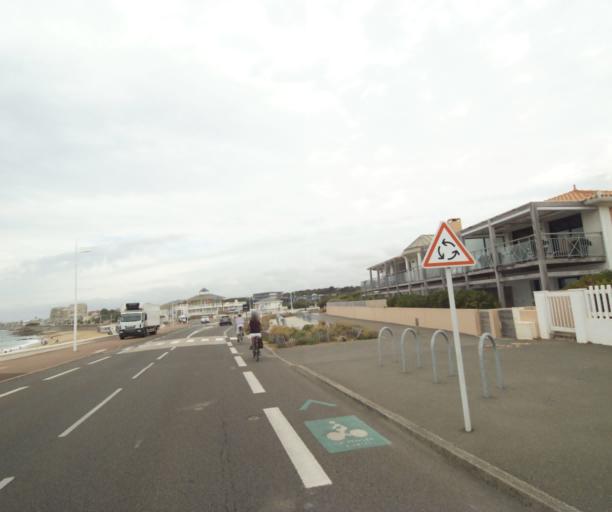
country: FR
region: Pays de la Loire
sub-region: Departement de la Vendee
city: Les Sables-d'Olonne
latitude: 46.4795
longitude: -1.7604
